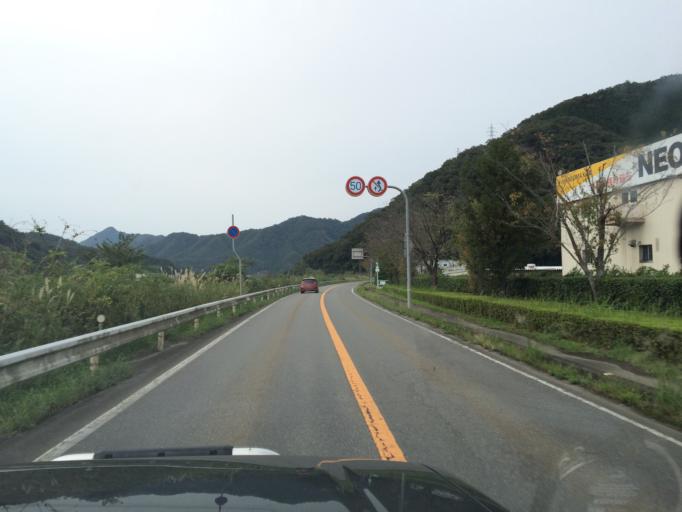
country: JP
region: Hyogo
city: Toyooka
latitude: 35.3935
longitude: 134.7937
